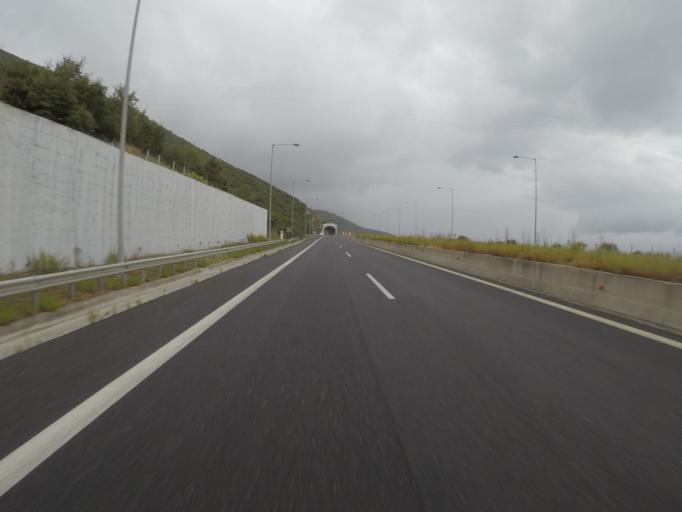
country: GR
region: Peloponnese
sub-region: Nomos Arkadias
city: Megalopoli
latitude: 37.3913
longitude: 22.1864
